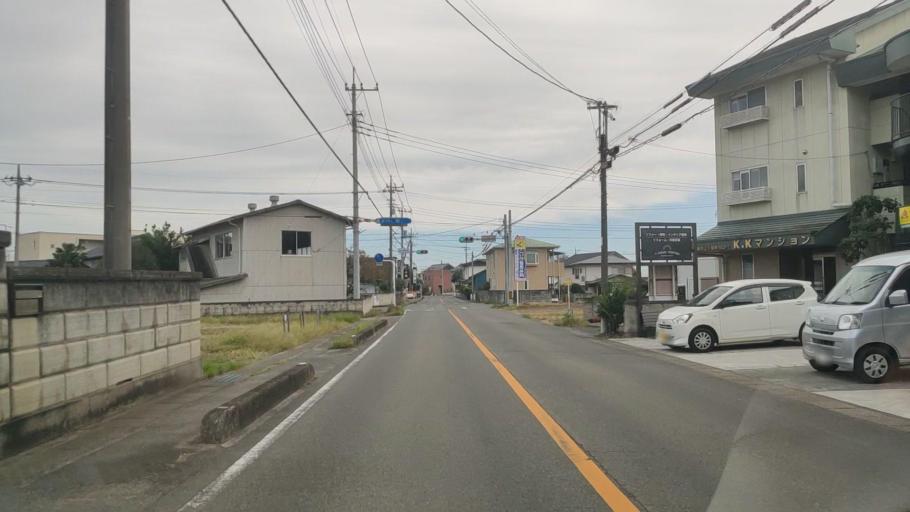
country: JP
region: Gunma
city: Takasaki
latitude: 36.3600
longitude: 138.9860
